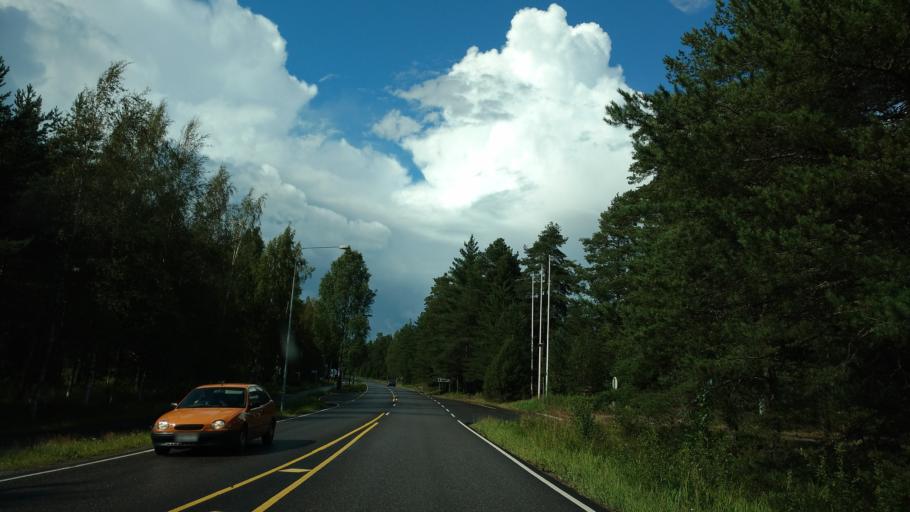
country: FI
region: Varsinais-Suomi
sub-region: Turku
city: Paimio
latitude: 60.4302
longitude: 22.7220
